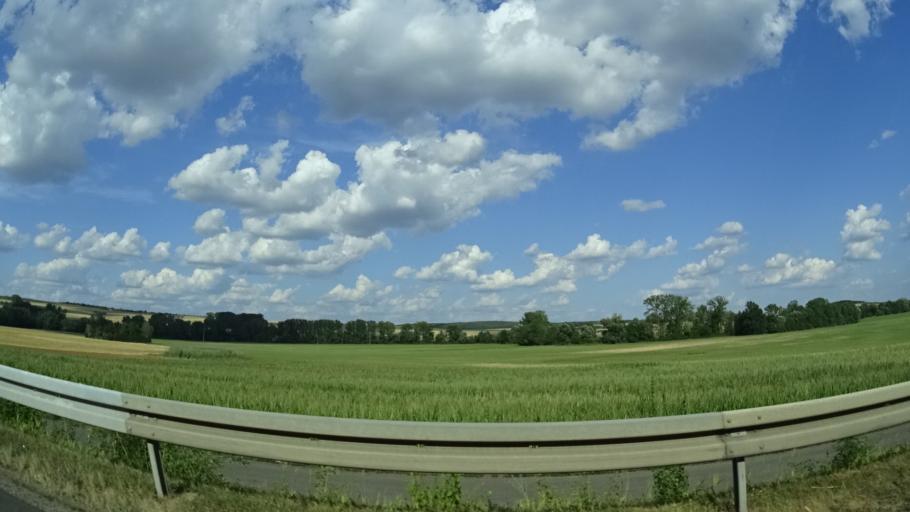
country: DE
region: Bavaria
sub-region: Regierungsbezirk Unterfranken
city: Wuelfershausen
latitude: 50.3233
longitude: 10.3439
